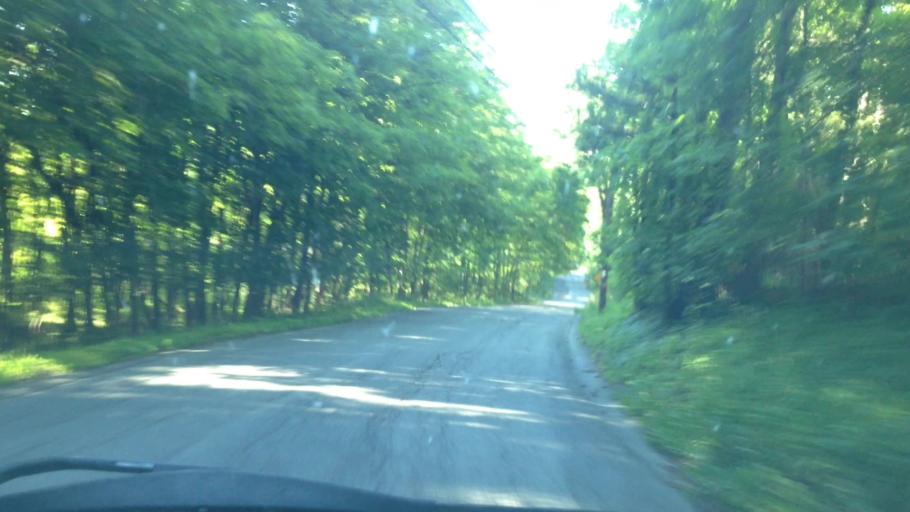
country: US
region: New York
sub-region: Ulster County
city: Tillson
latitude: 41.8186
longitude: -74.0457
